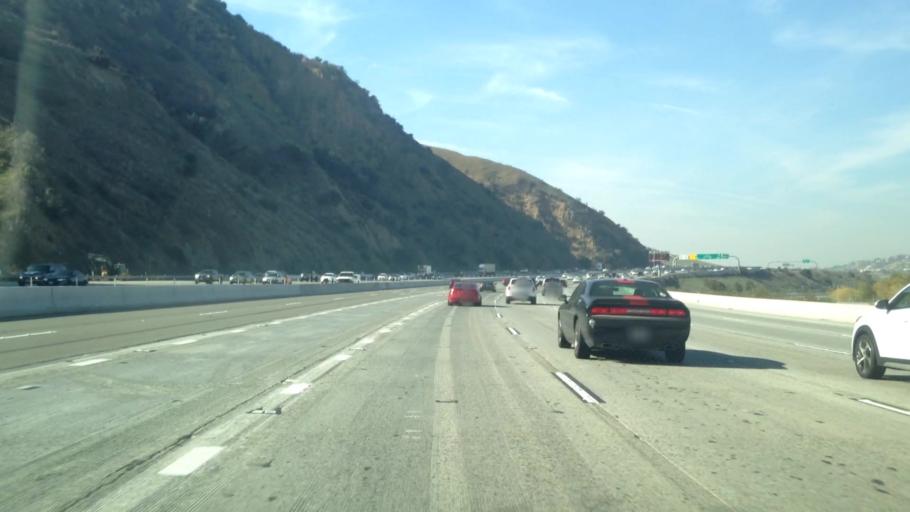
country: US
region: California
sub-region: San Bernardino County
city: Los Serranos
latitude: 33.8689
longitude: -117.6766
